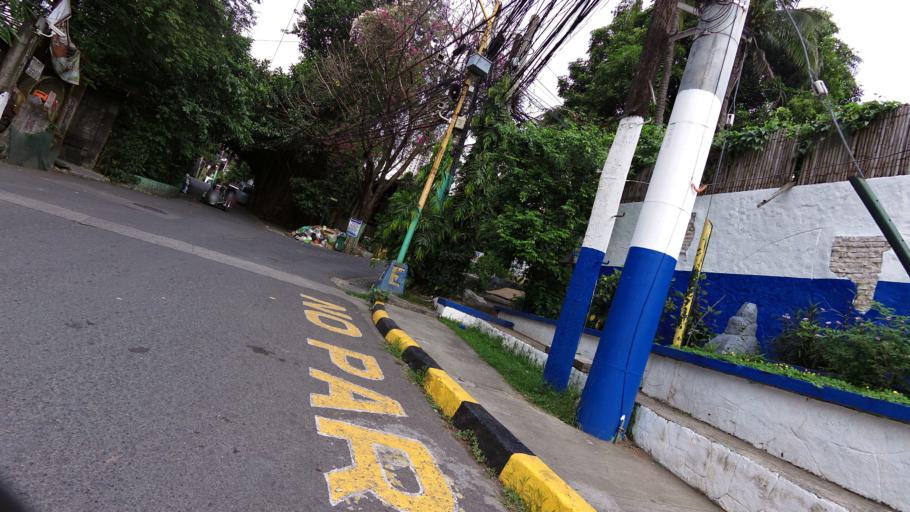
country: PH
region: Metro Manila
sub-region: Pasig
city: Pasig City
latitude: 14.5663
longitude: 121.0586
